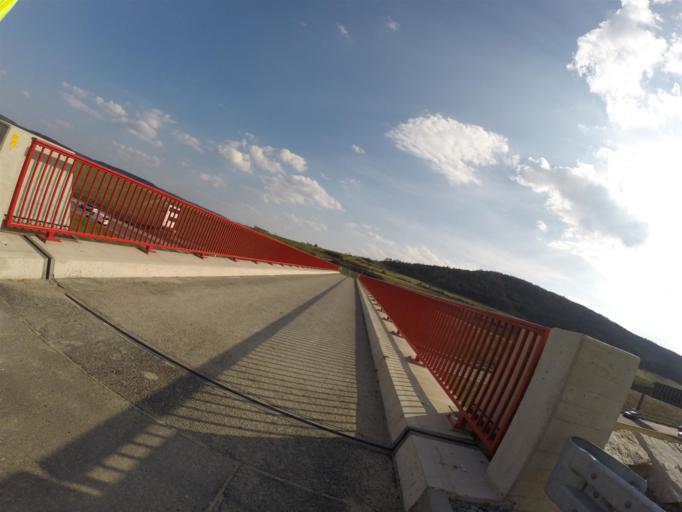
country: DE
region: Thuringia
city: Rothenstein
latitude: 50.8707
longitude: 11.5857
